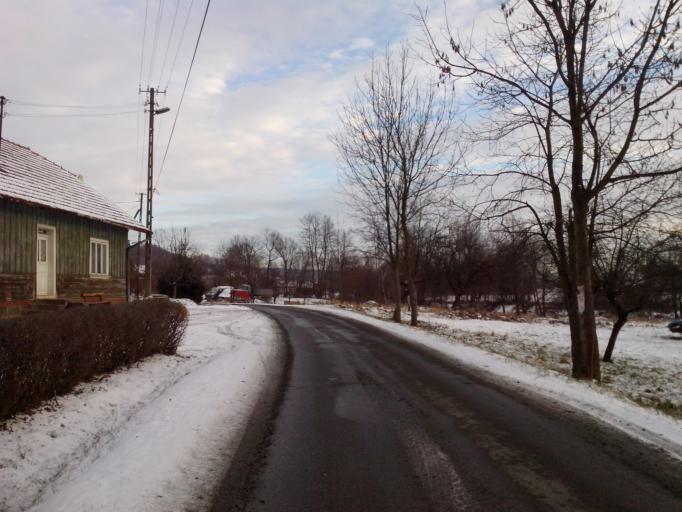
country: PL
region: Subcarpathian Voivodeship
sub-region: Powiat strzyzowski
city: Strzyzow
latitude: 49.8509
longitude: 21.8078
